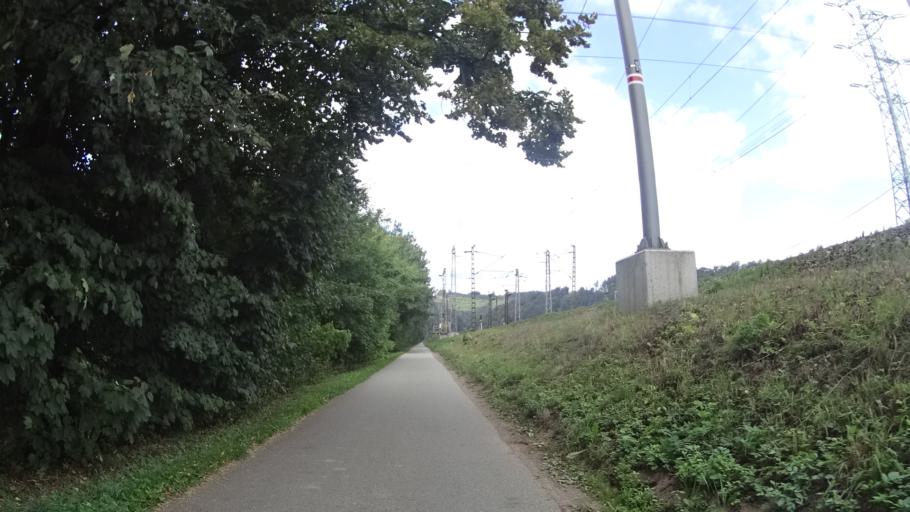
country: CZ
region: Pardubicky
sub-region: Okres Usti nad Orlici
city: Usti nad Orlici
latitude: 49.9730
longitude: 16.3569
